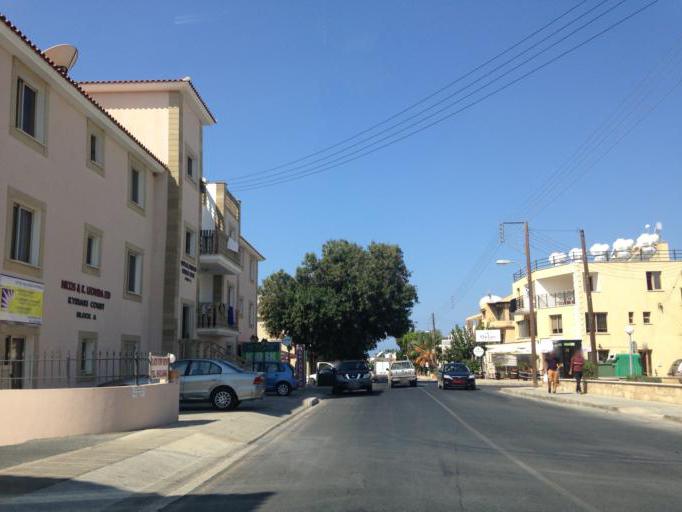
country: CY
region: Pafos
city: Chlorakas
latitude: 34.8033
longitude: 32.4053
